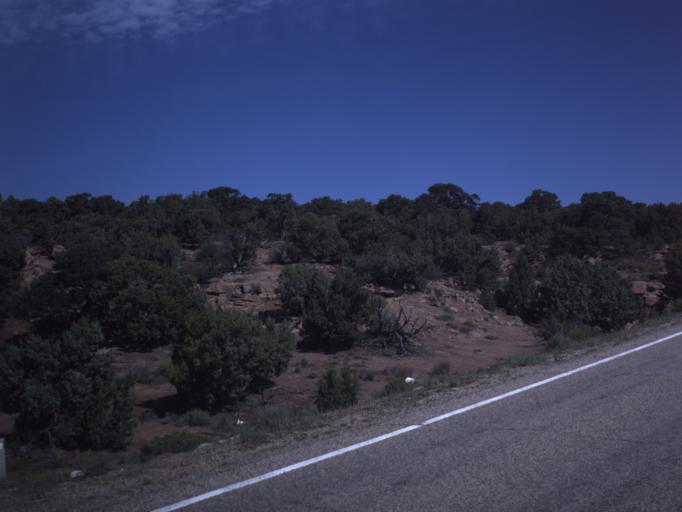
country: US
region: Utah
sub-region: Duchesne County
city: Duchesne
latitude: 40.2989
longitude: -110.3736
